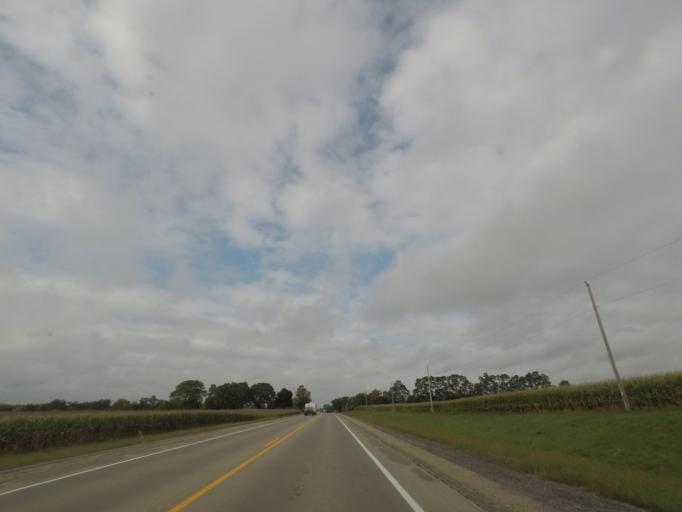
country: US
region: Wisconsin
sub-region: Dane County
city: Deerfield
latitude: 43.0325
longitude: -89.1372
